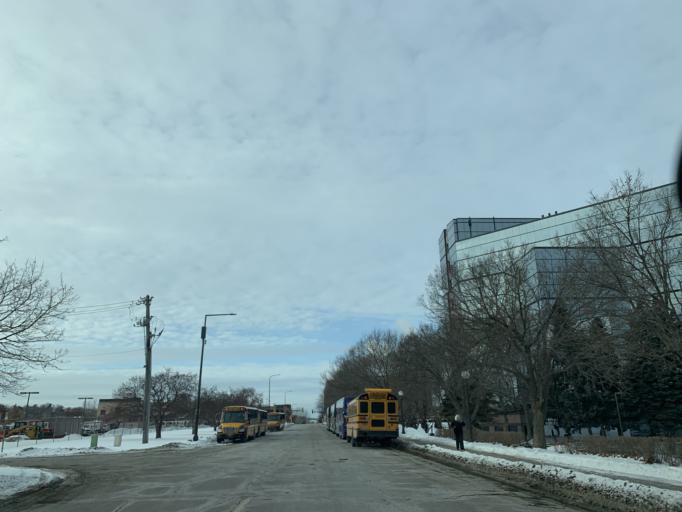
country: US
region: Minnesota
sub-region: Ramsey County
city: Saint Paul
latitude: 44.9427
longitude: -93.0821
